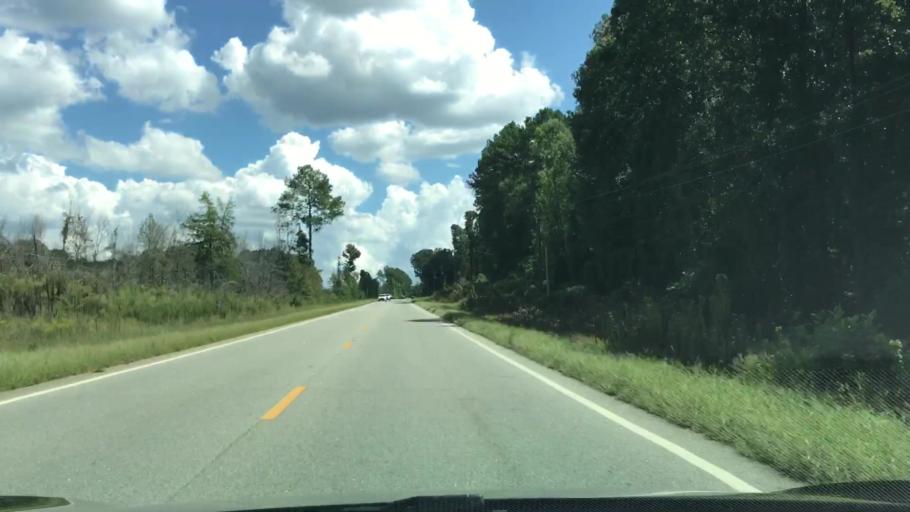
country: US
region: Georgia
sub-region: Greene County
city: Greensboro
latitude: 33.6100
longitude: -83.2049
